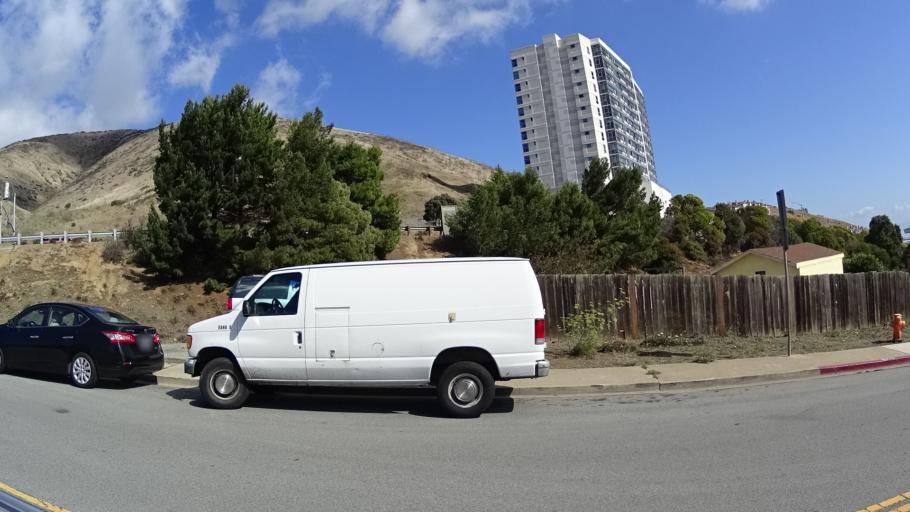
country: US
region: California
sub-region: San Mateo County
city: South San Francisco
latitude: 37.6655
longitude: -122.4053
